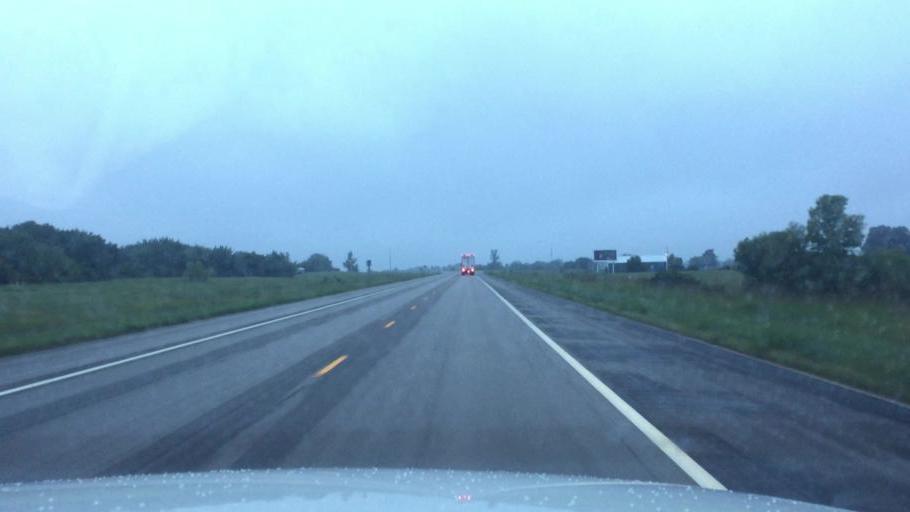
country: US
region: Kansas
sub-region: Montgomery County
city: Cherryvale
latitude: 37.4602
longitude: -95.4806
